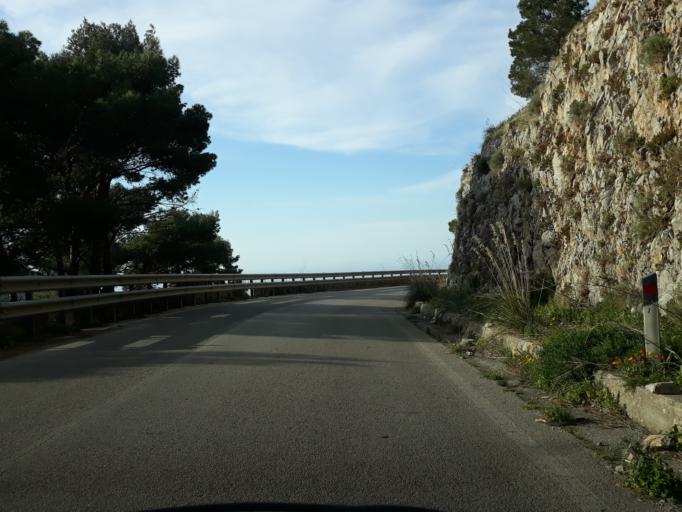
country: IT
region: Sicily
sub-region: Palermo
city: Torretta
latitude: 38.1185
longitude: 13.2429
